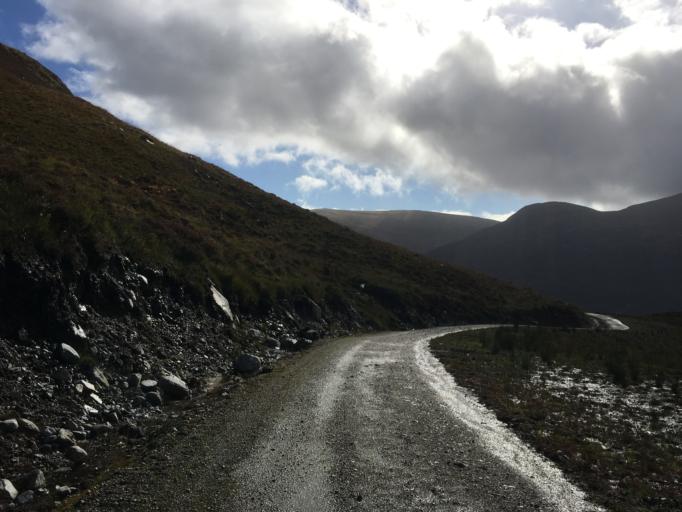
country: GB
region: Scotland
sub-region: Highland
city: Spean Bridge
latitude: 57.3478
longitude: -4.9822
